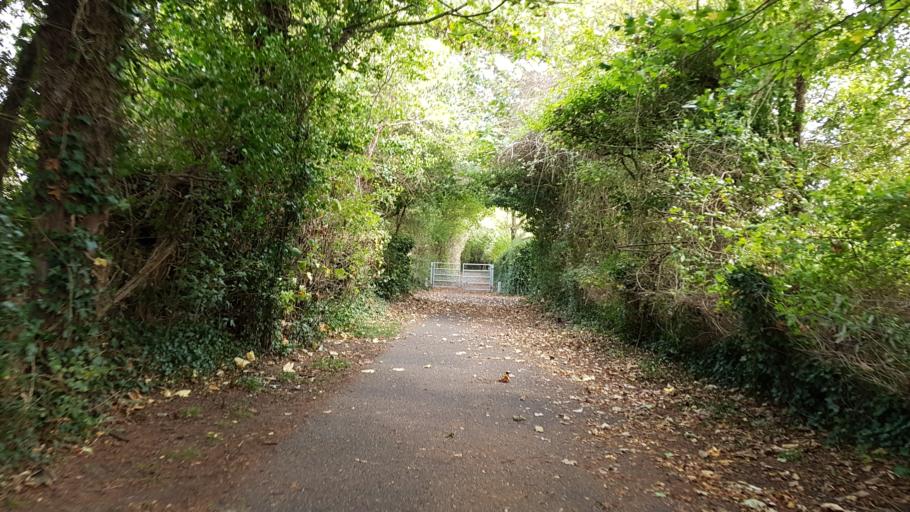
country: GB
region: England
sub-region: Isle of Wight
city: Ryde
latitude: 50.7299
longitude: -1.1780
